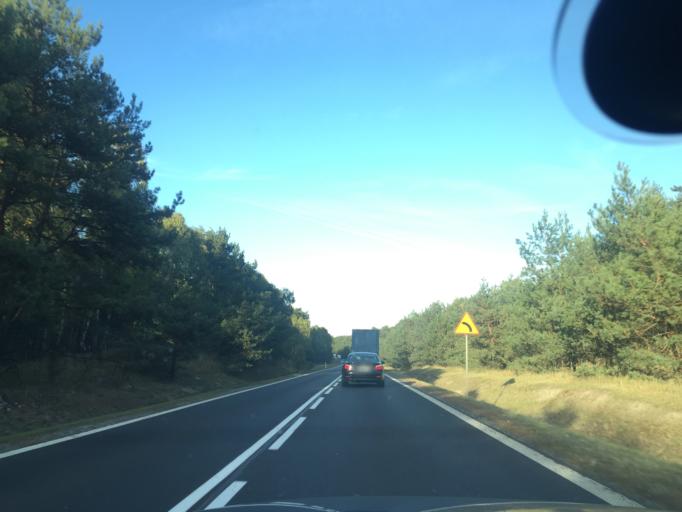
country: PL
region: Kujawsko-Pomorskie
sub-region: Powiat torunski
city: Wielka Nieszawka
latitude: 52.9452
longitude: 18.5219
